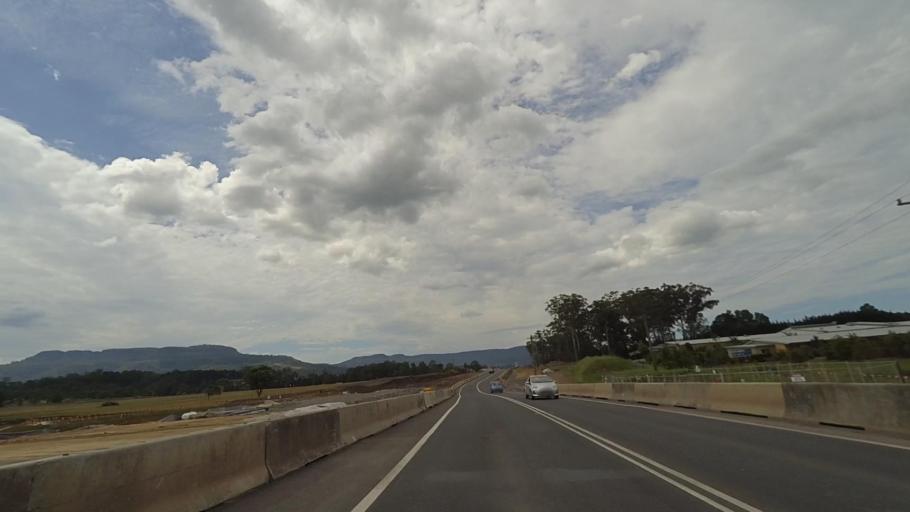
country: AU
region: New South Wales
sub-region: Shoalhaven Shire
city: Berry
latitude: -34.7803
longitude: 150.6808
